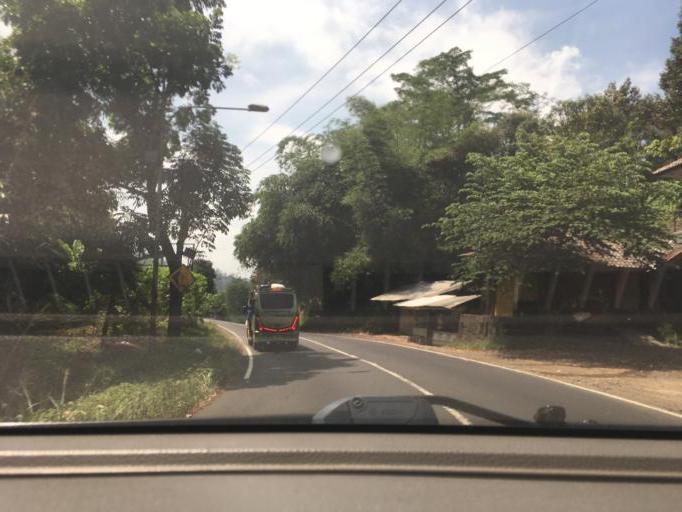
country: ID
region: West Java
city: Wage Cibahayu
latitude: -7.1164
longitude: 108.1194
